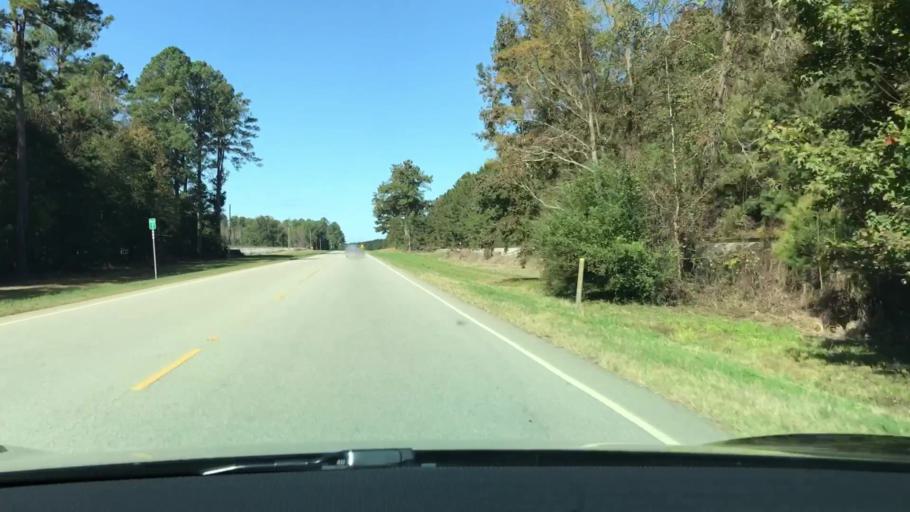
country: US
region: Georgia
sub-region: Warren County
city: Firing Range
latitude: 33.4721
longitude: -82.7231
